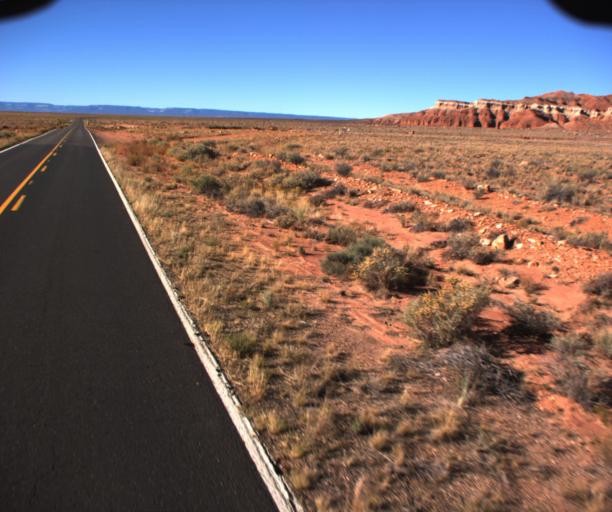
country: US
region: Arizona
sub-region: Coconino County
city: LeChee
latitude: 36.7117
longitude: -111.7795
